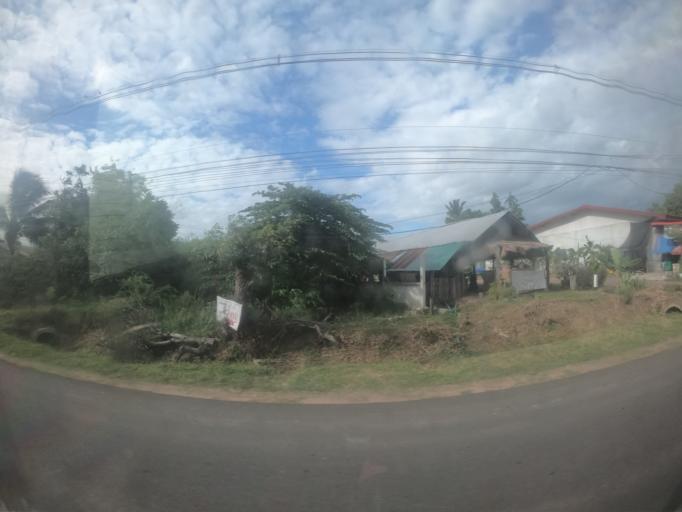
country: TH
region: Surin
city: Prasat
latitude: 14.6062
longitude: 103.4249
